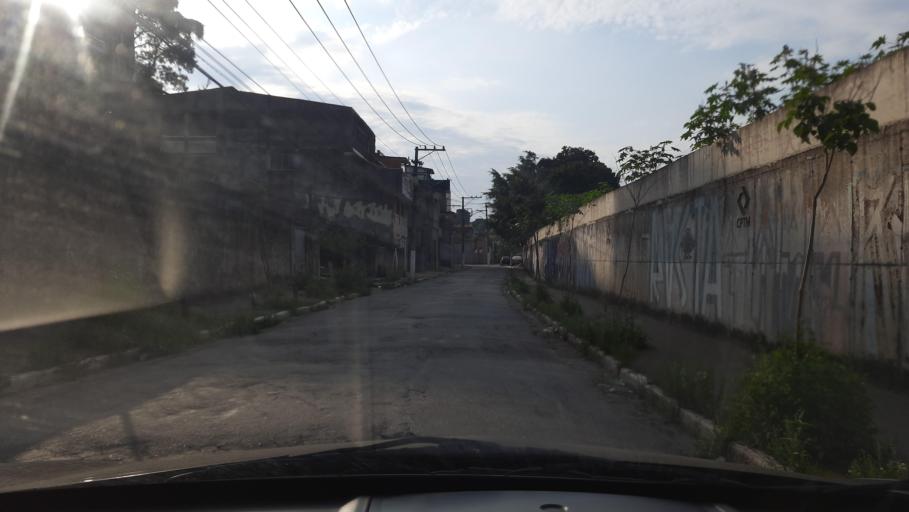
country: BR
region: Sao Paulo
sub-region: Caieiras
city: Caieiras
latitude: -23.4418
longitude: -46.7450
